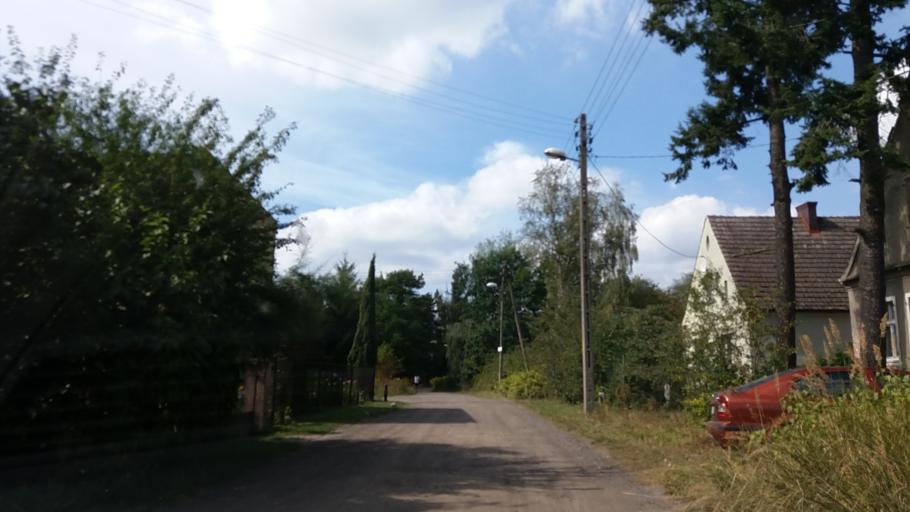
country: PL
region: West Pomeranian Voivodeship
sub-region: Powiat stargardzki
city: Kobylanka
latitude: 53.3565
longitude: 14.9199
